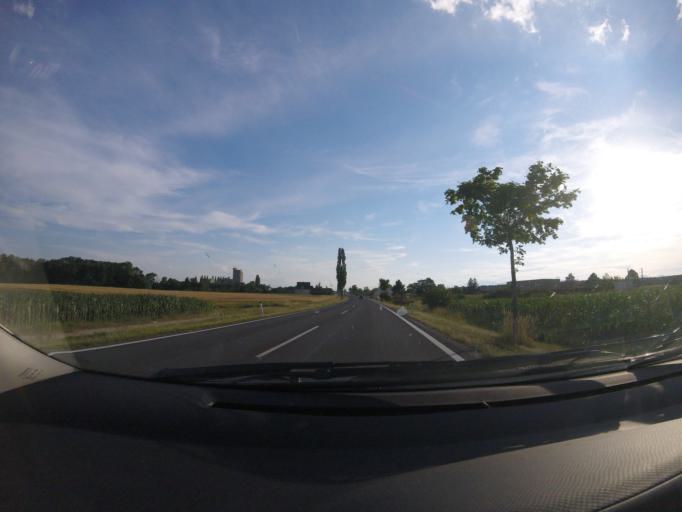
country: AT
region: Lower Austria
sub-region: Politischer Bezirk Wiener Neustadt
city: Lichtenworth
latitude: 47.8441
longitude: 16.2880
